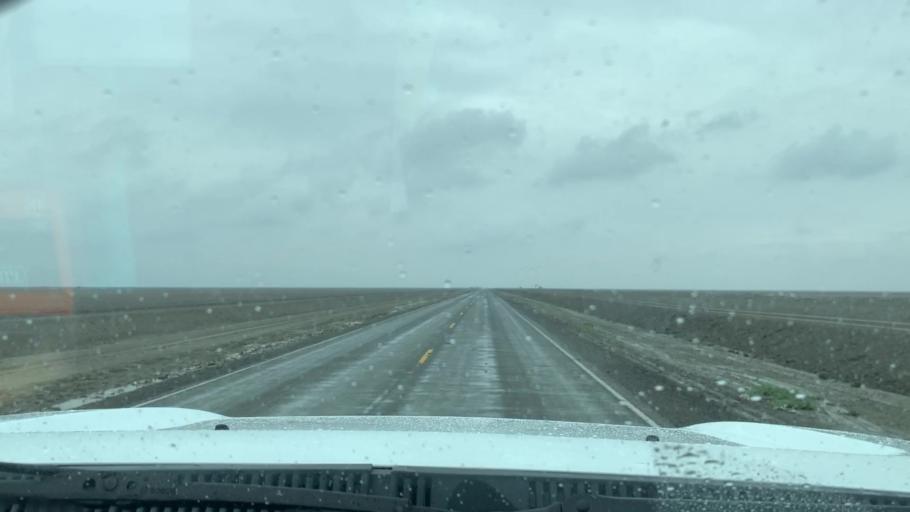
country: US
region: California
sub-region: Tulare County
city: Alpaugh
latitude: 35.9344
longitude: -119.5773
